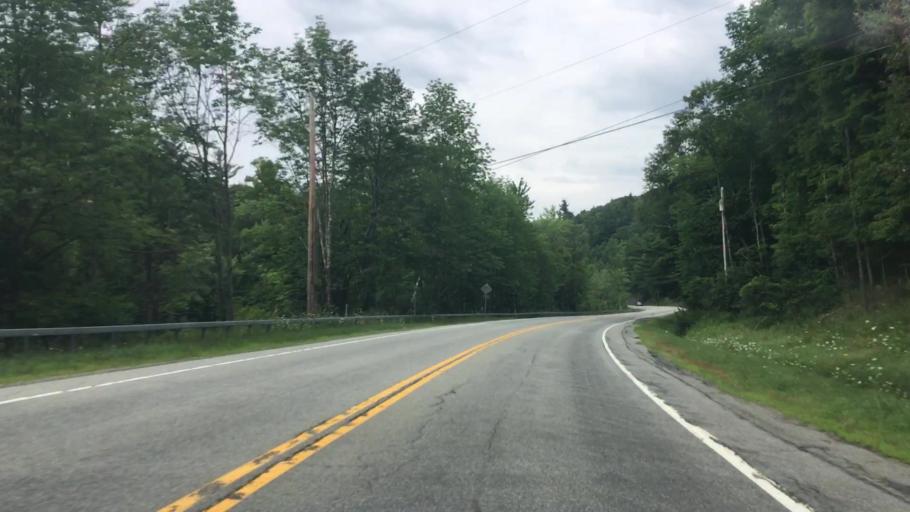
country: US
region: New York
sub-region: Essex County
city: Lake Placid
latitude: 44.2800
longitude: -73.7896
